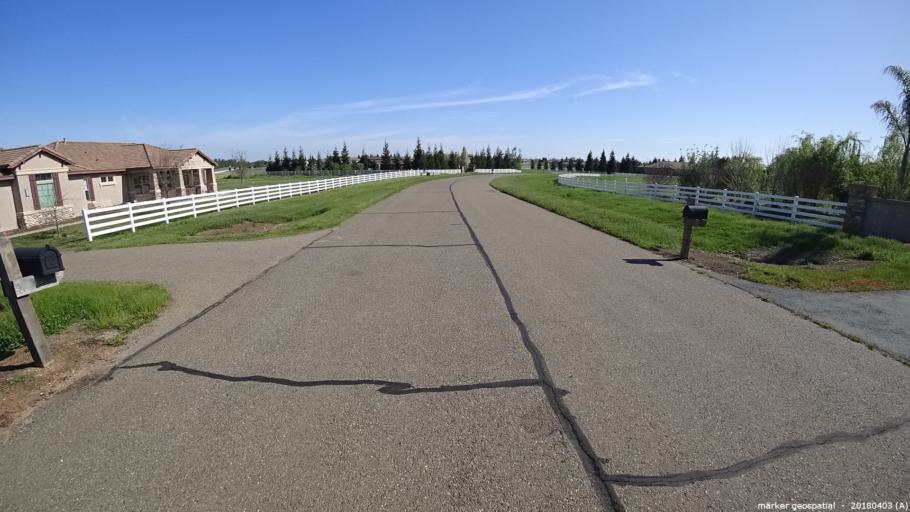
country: US
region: California
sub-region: Sacramento County
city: Wilton
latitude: 38.4124
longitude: -121.2026
